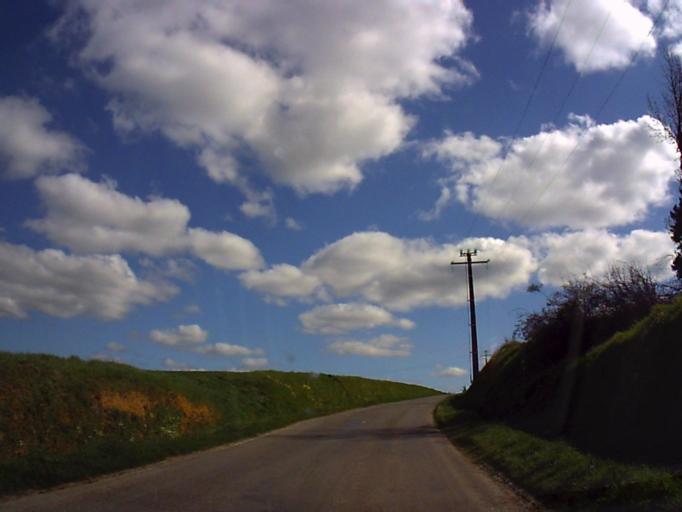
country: FR
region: Brittany
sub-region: Departement d'Ille-et-Vilaine
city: Boisgervilly
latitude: 48.1015
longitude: -2.1183
